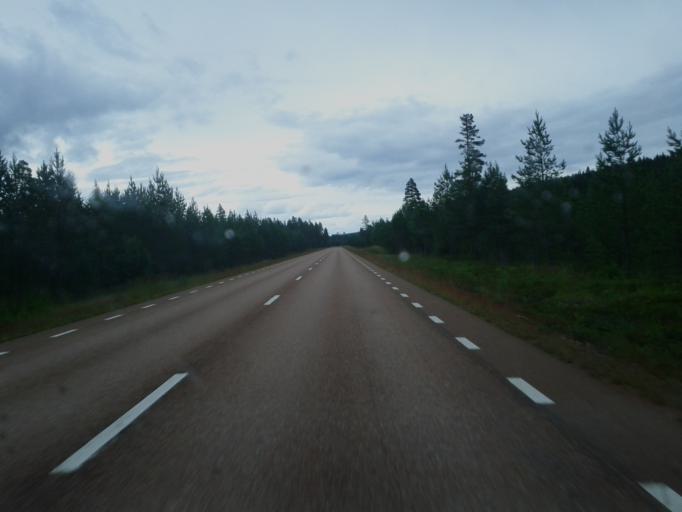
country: SE
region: Dalarna
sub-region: Alvdalens Kommun
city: AElvdalen
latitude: 61.2782
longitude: 13.8713
